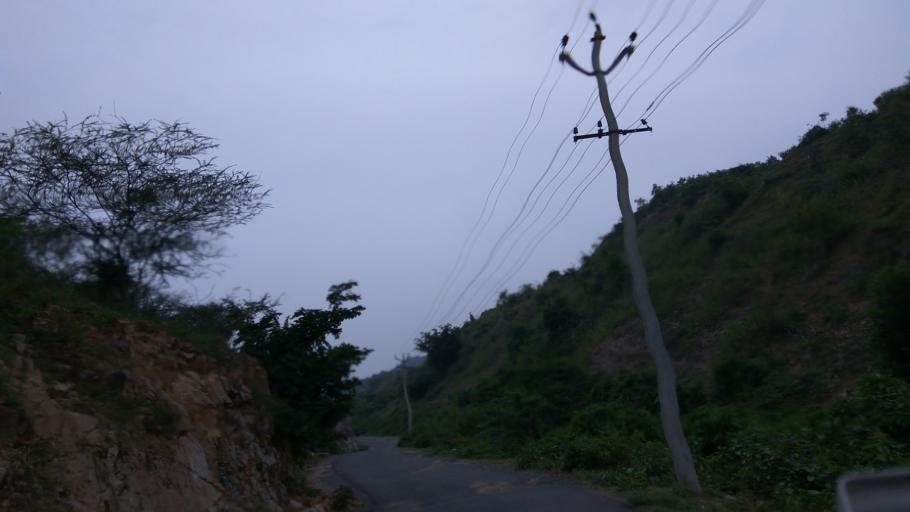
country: IN
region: Tamil Nadu
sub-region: Dharmapuri
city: Dharmapuri
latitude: 12.0177
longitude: 78.1234
